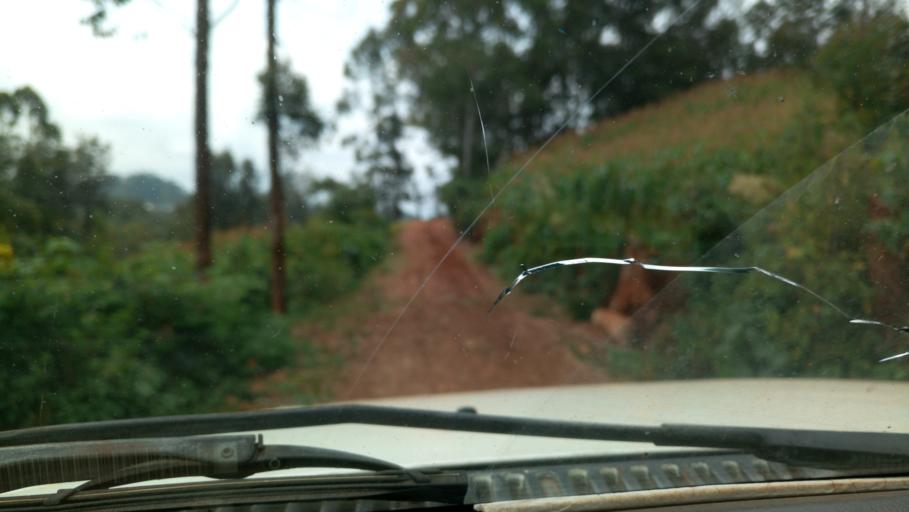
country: KE
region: Nyeri
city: Othaya
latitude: -0.5882
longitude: 37.0116
